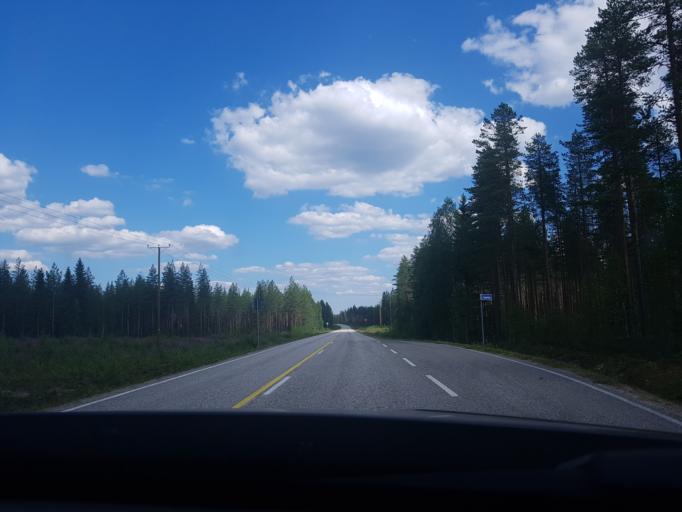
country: FI
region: Kainuu
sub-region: Kehys-Kainuu
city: Kuhmo
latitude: 64.2072
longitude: 29.7419
